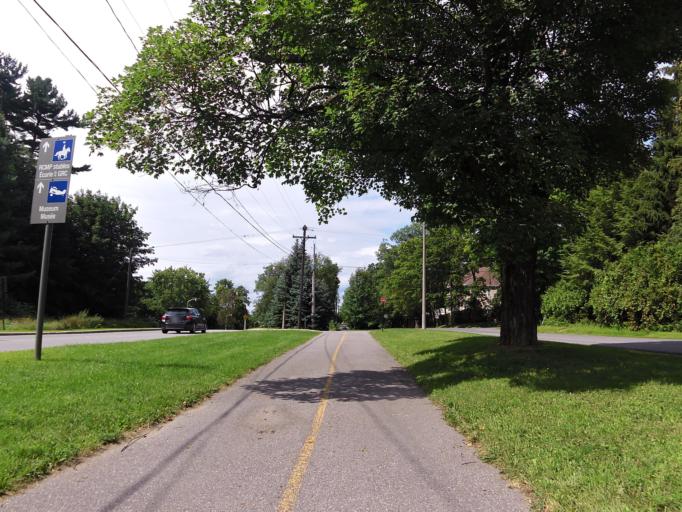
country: CA
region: Quebec
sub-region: Outaouais
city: Gatineau
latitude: 45.4499
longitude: -75.6858
